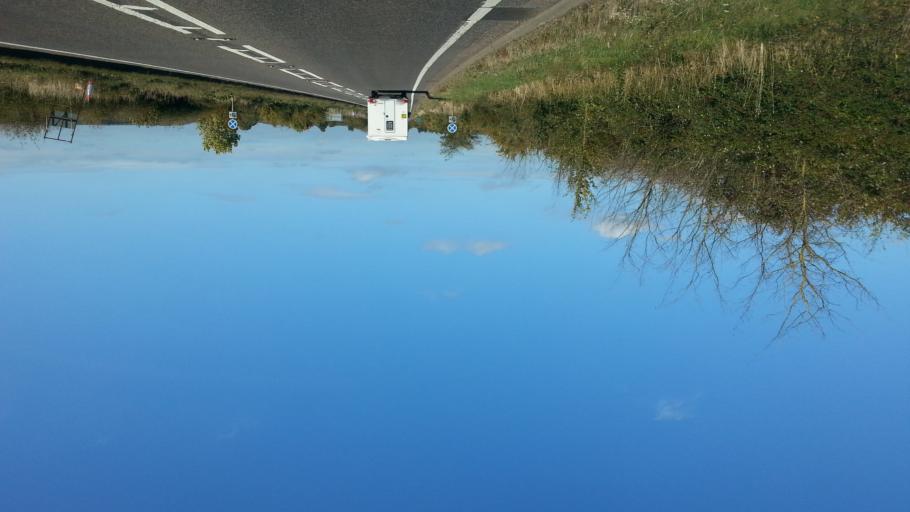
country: GB
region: England
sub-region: Northamptonshire
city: Oundle
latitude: 52.5011
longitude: -0.4379
